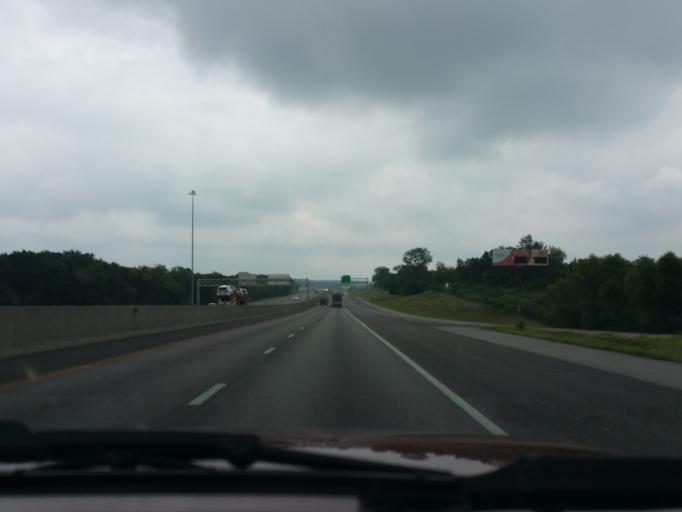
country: US
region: Kansas
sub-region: Wyandotte County
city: Edwardsville
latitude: 39.1060
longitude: -94.8330
